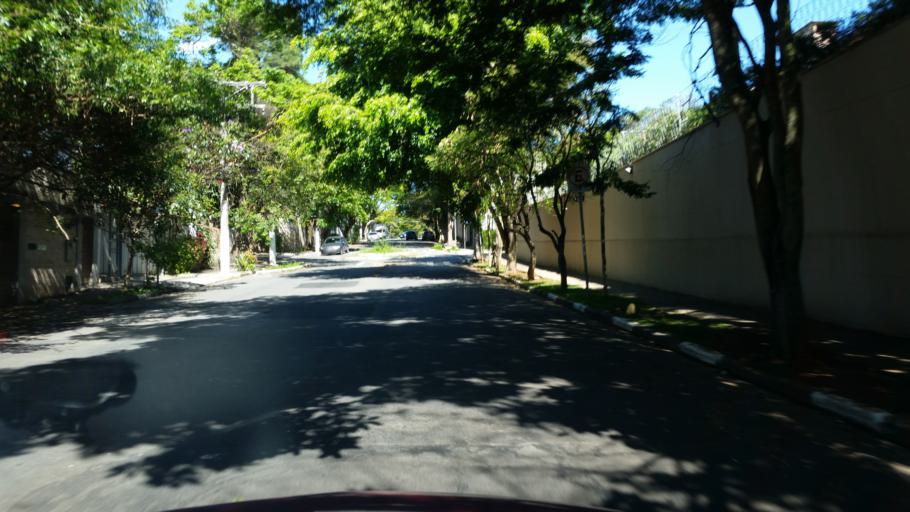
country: BR
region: Sao Paulo
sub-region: Diadema
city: Diadema
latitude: -23.6432
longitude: -46.6921
